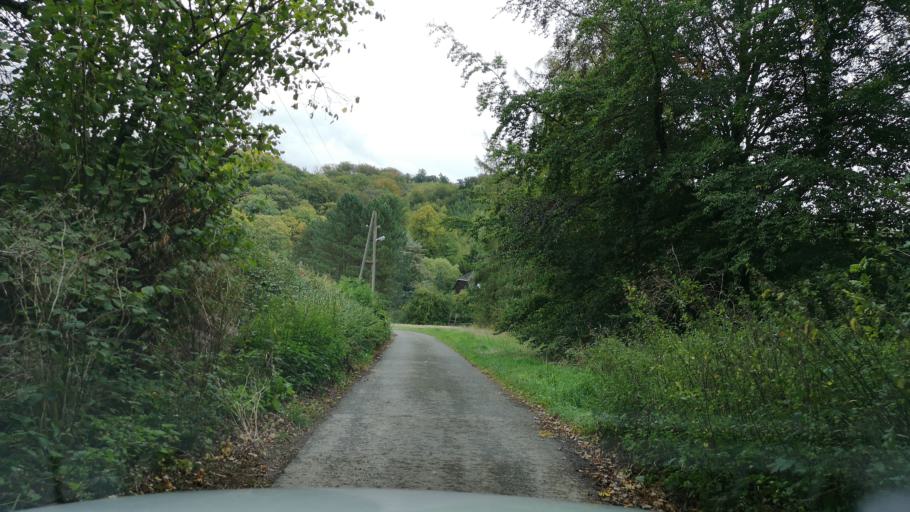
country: DE
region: North Rhine-Westphalia
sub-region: Regierungsbezirk Dusseldorf
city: Velbert
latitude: 51.3751
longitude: 7.0357
